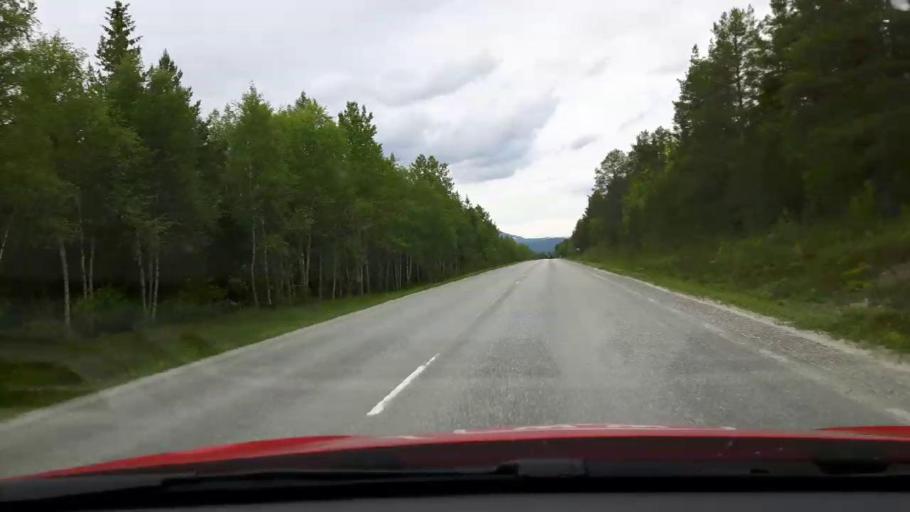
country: NO
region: Hedmark
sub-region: Engerdal
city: Engerdal
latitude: 62.5293
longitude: 12.5722
